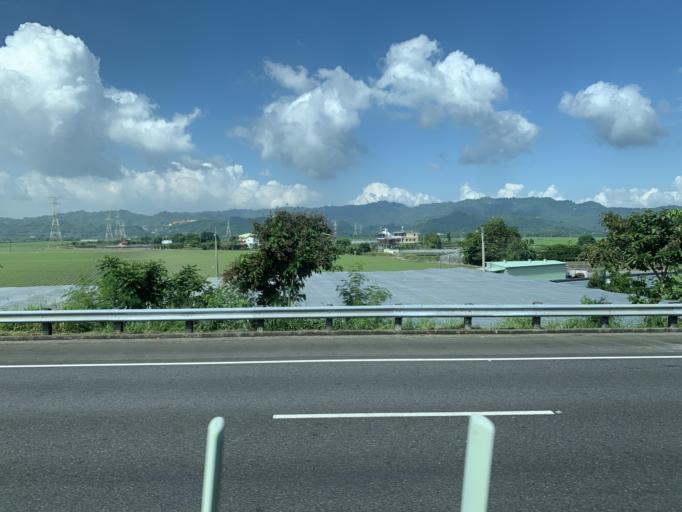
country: TW
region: Taiwan
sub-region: Pingtung
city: Pingtung
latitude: 22.8181
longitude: 120.4868
